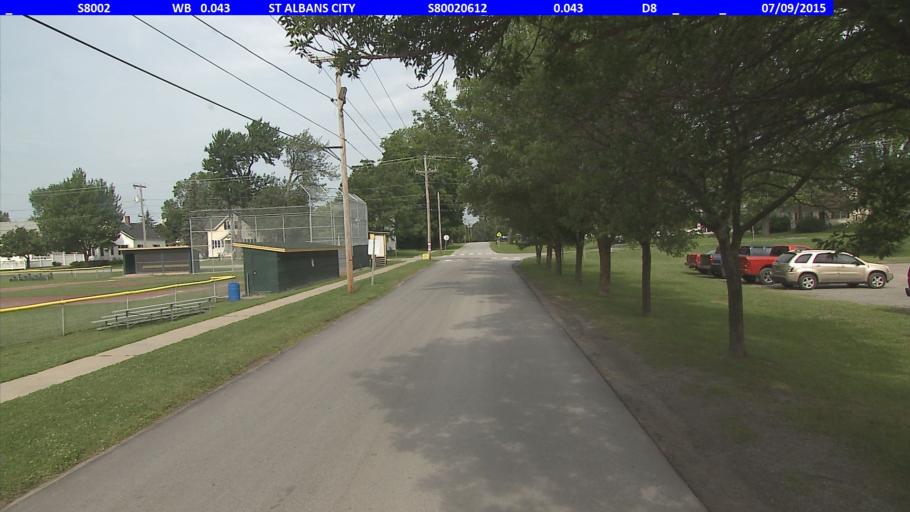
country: US
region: Vermont
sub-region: Franklin County
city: Saint Albans
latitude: 44.8182
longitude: -73.0895
